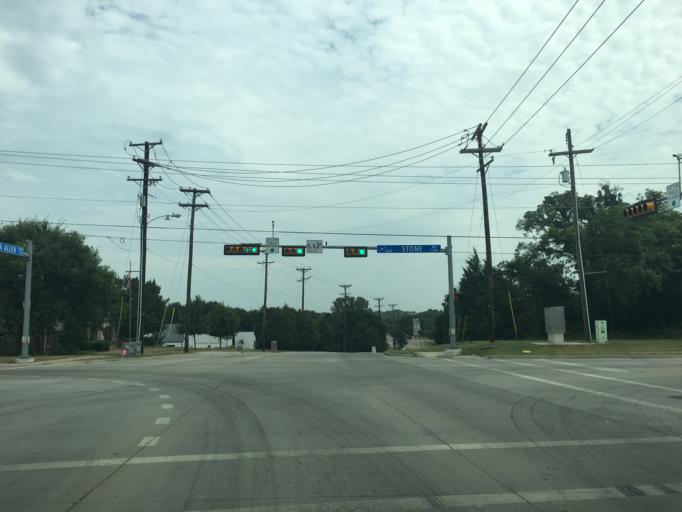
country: US
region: Texas
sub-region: Collin County
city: Wylie
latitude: 33.0056
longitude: -96.5221
